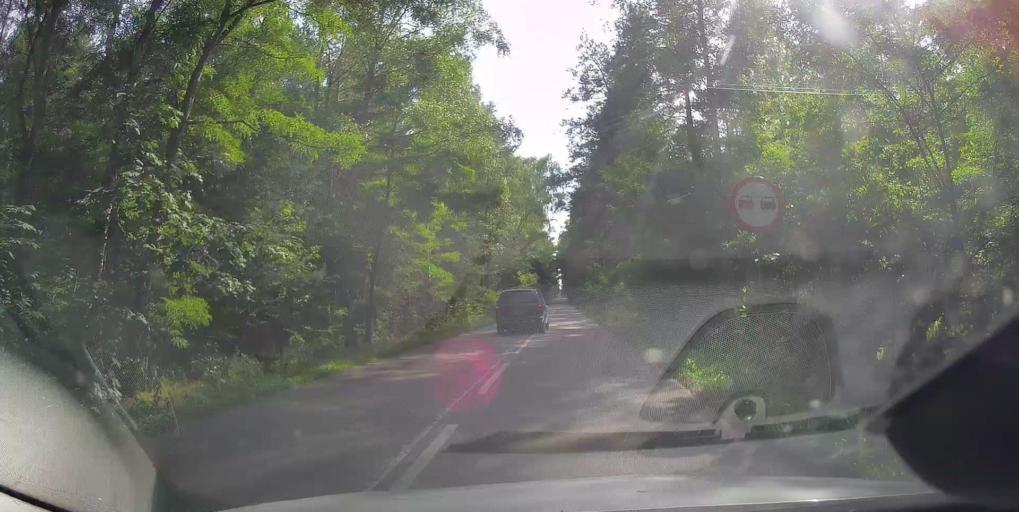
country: PL
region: Lodz Voivodeship
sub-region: Powiat opoczynski
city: Mniszkow
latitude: 51.4077
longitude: 20.0464
